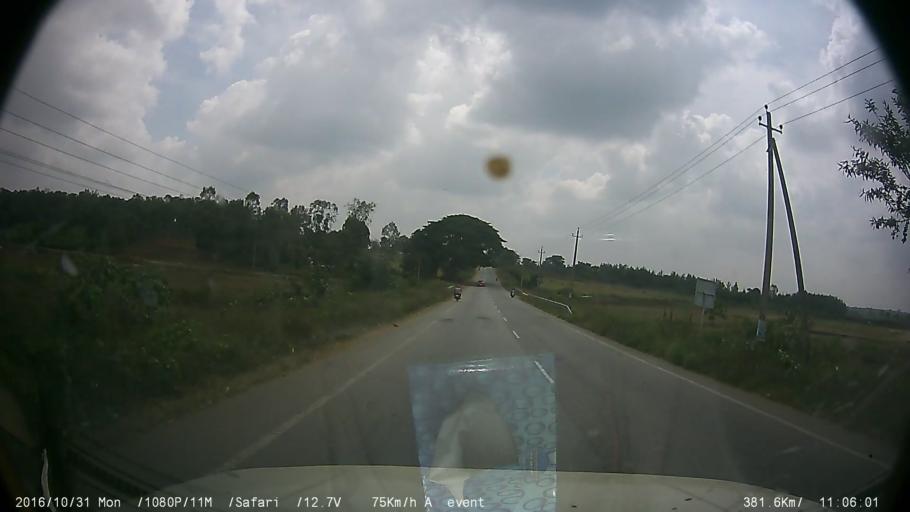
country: IN
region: Karnataka
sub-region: Mysore
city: Piriyapatna
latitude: 12.3769
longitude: 76.0386
